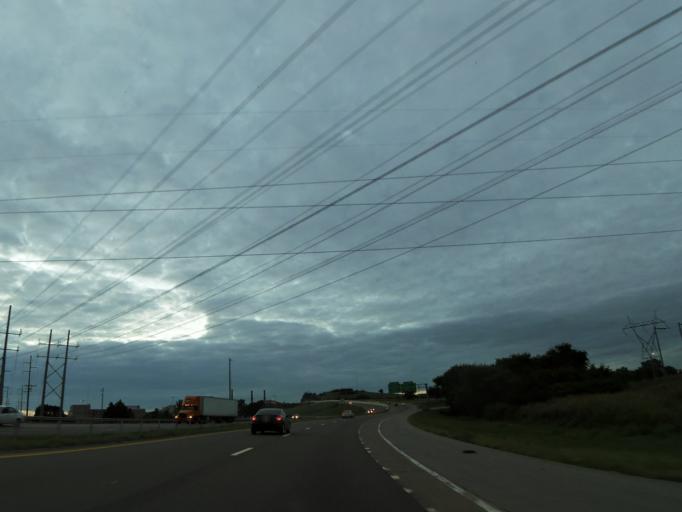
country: US
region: Tennessee
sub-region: Davidson County
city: Belle Meade
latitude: 36.1669
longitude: -86.8695
